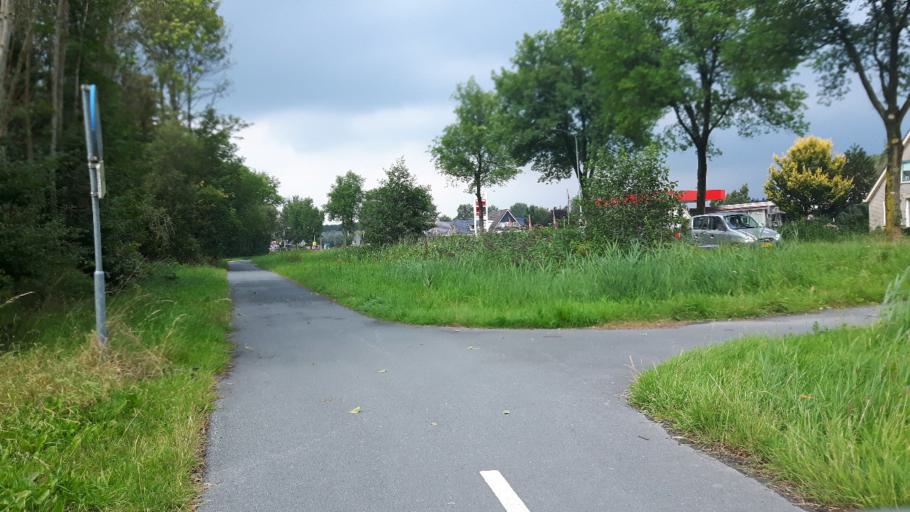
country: NL
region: Groningen
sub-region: Gemeente Bedum
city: Bedum
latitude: 53.3414
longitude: 6.6489
